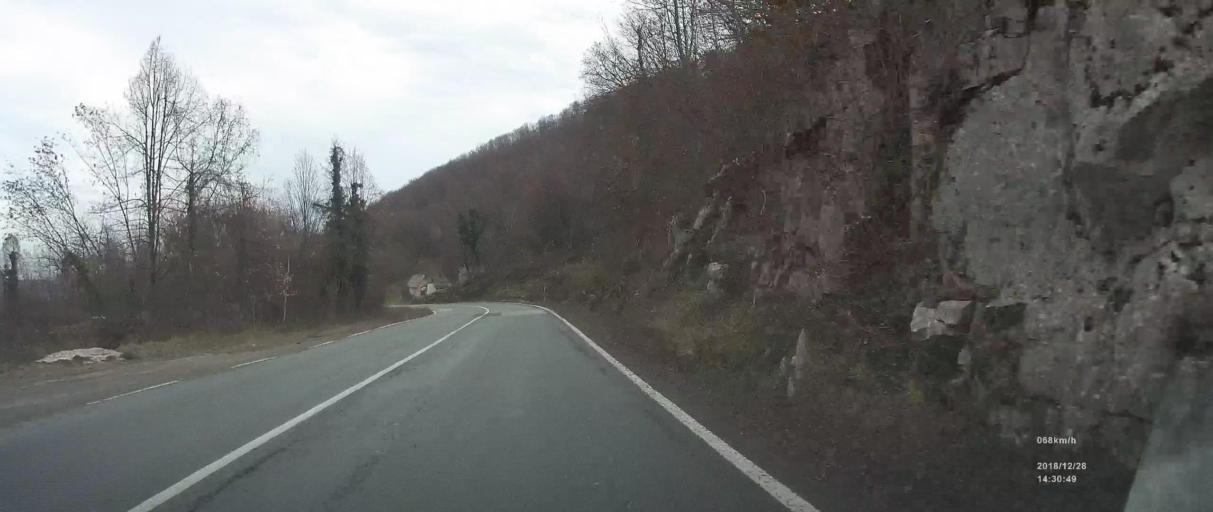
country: HR
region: Primorsko-Goranska
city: Vrbovsko
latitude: 45.4177
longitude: 15.1342
